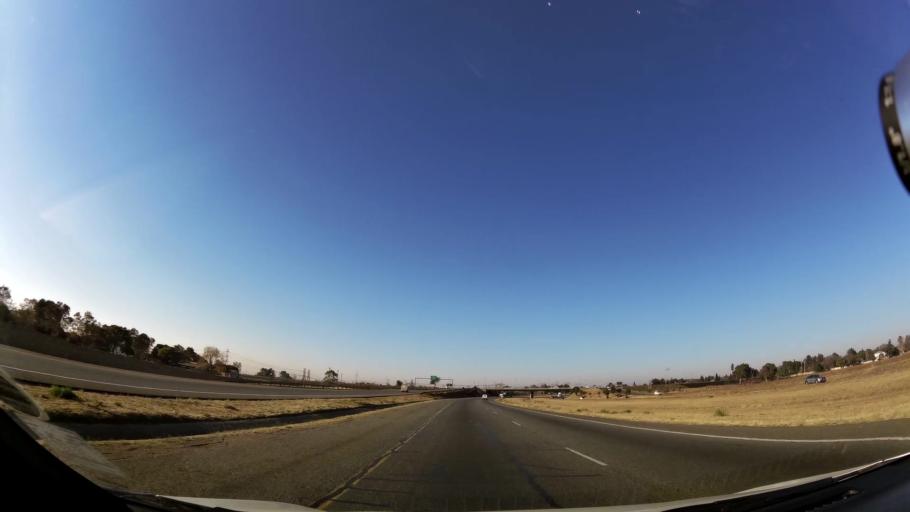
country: ZA
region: Gauteng
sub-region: Ekurhuleni Metropolitan Municipality
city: Germiston
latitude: -26.3025
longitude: 28.1108
